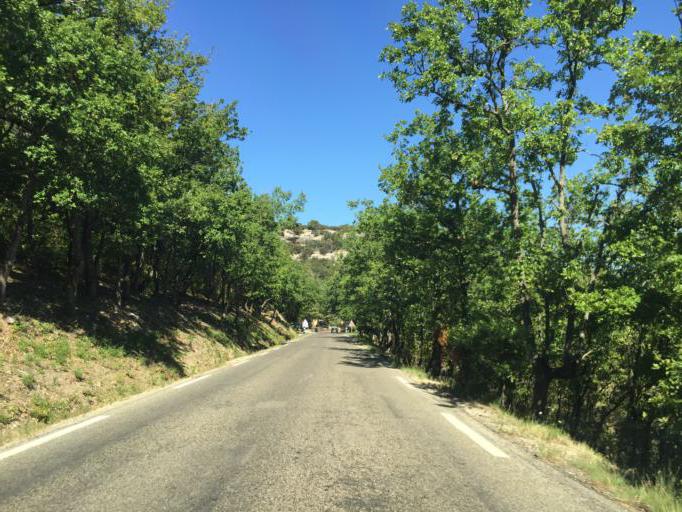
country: FR
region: Provence-Alpes-Cote d'Azur
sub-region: Departement du Vaucluse
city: Venasque
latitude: 43.9987
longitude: 5.1466
